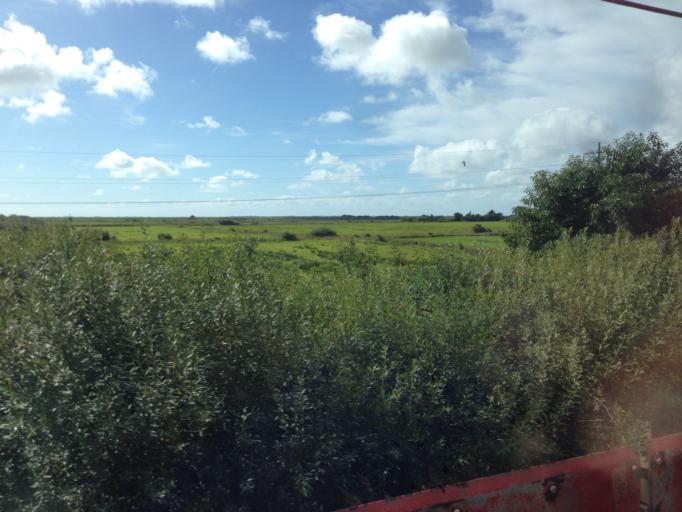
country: DE
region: Schleswig-Holstein
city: Keitum
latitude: 54.8851
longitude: 8.3789
